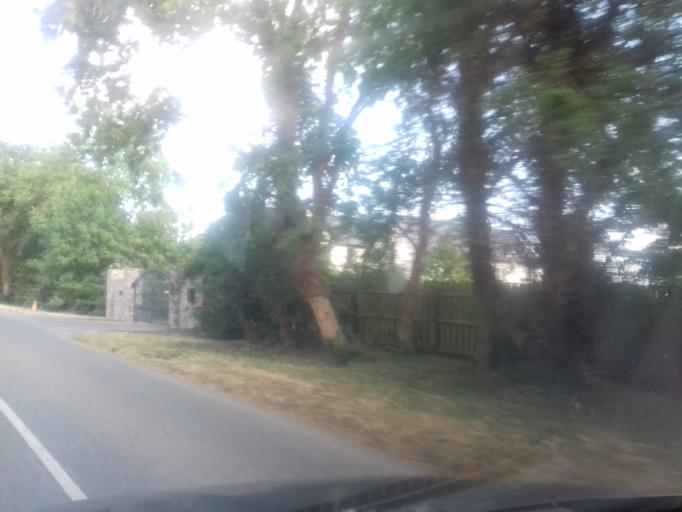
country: IE
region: Leinster
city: Hartstown
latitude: 53.4454
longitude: -6.4353
